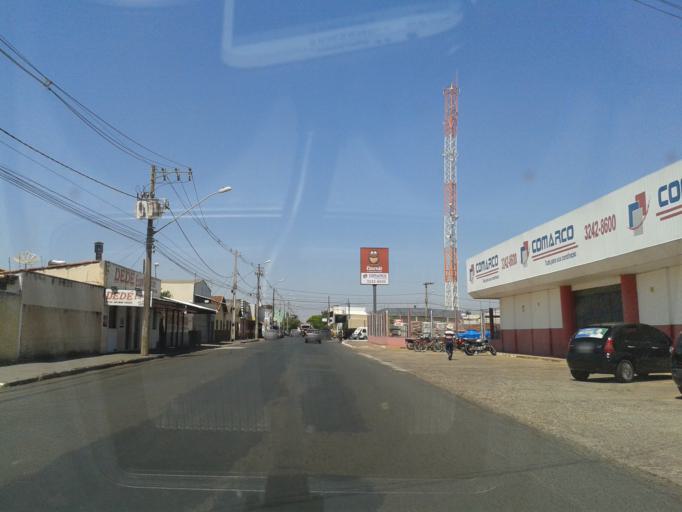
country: BR
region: Minas Gerais
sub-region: Araguari
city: Araguari
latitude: -18.6666
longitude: -48.1822
